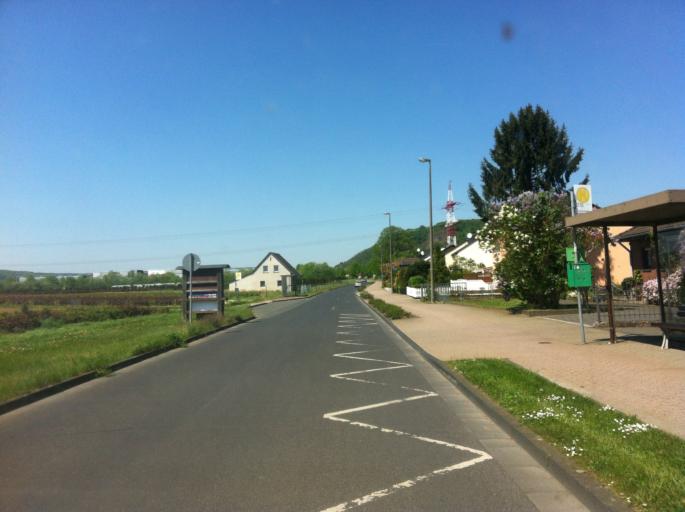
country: DE
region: Rheinland-Pfalz
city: Kasbach-Ohlenberg
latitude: 50.5696
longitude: 7.2589
